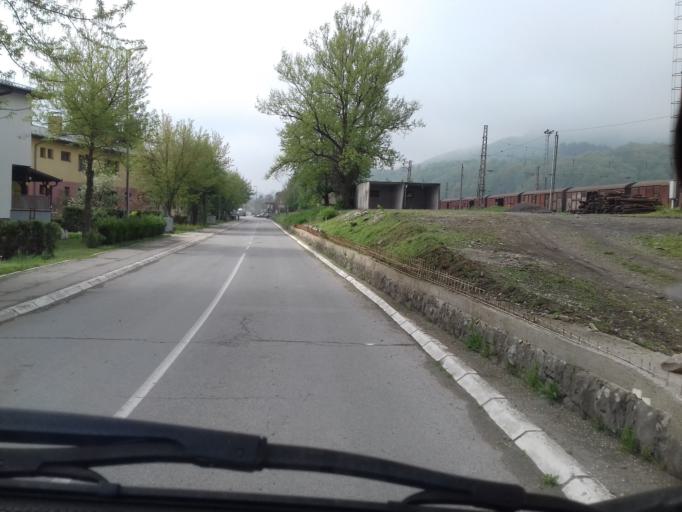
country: BA
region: Federation of Bosnia and Herzegovina
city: Maglaj
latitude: 44.5482
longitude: 18.0945
